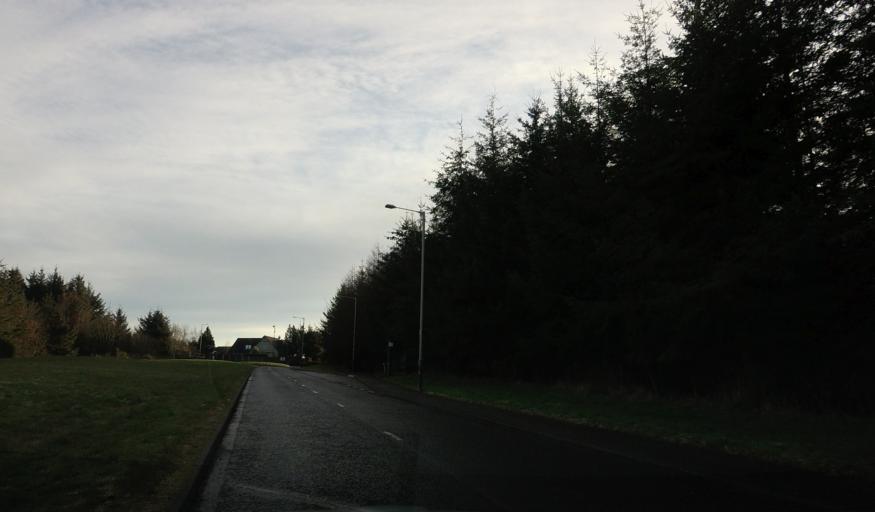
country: GB
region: Scotland
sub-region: Angus
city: Muirhead
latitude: 56.5045
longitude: -3.1318
